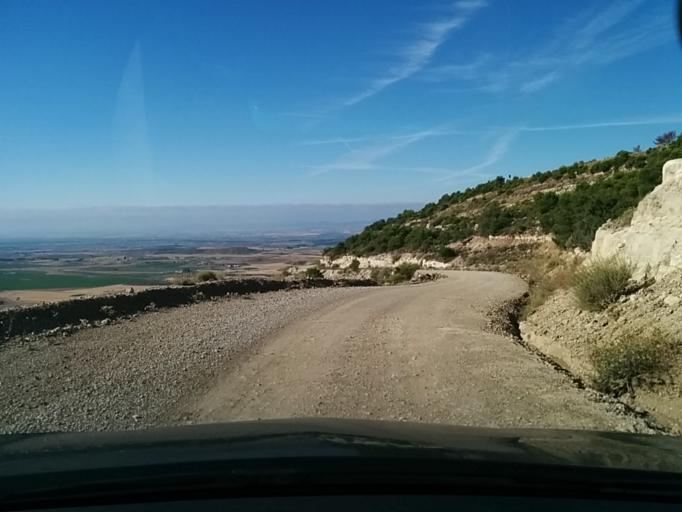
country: ES
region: Aragon
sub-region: Provincia de Zaragoza
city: Novillas
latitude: 42.0230
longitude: -1.3190
